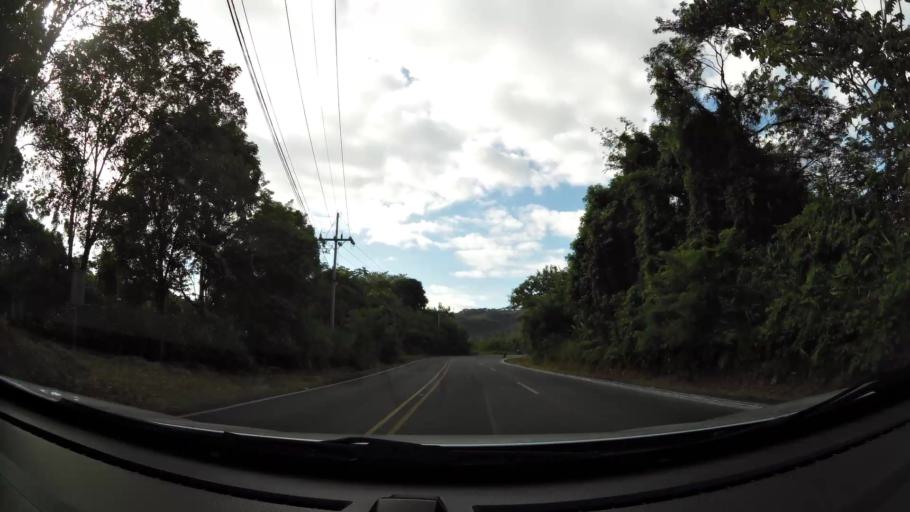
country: CR
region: Puntarenas
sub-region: Canton de Garabito
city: Jaco
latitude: 9.6749
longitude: -84.6424
